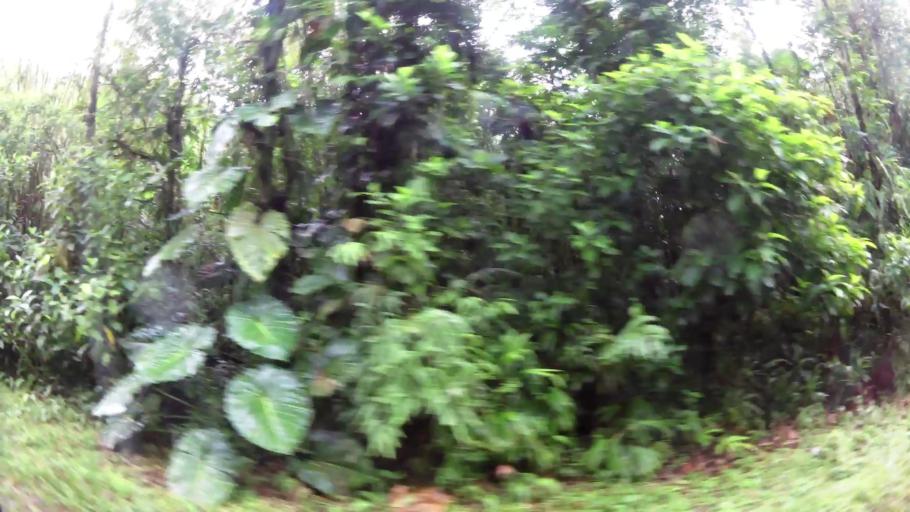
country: GP
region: Guadeloupe
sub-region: Guadeloupe
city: Trois-Rivieres
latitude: 16.0367
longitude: -61.6362
